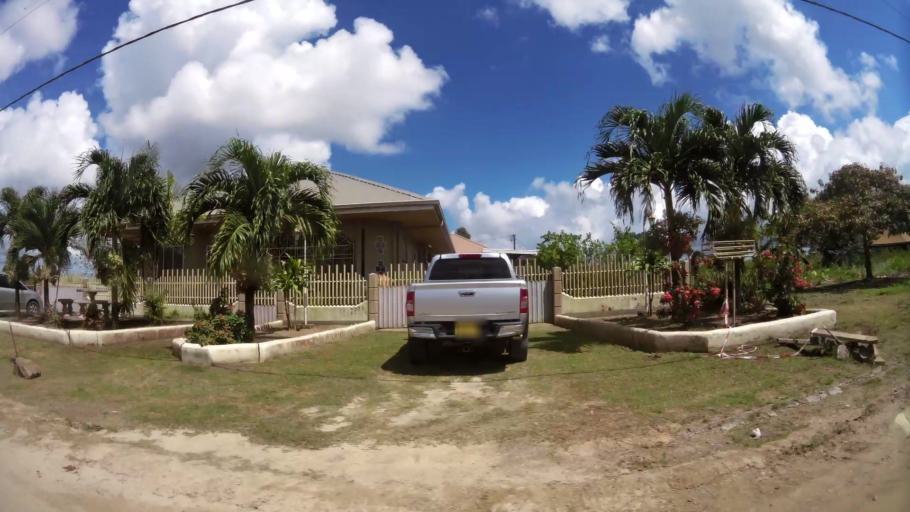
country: SR
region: Paramaribo
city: Paramaribo
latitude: 5.8638
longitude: -55.1314
